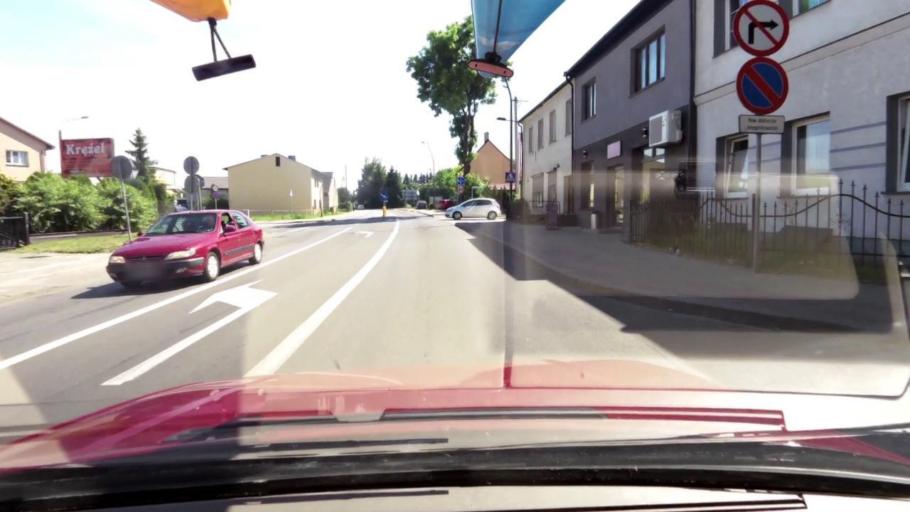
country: PL
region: Pomeranian Voivodeship
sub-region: Powiat slupski
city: Kobylnica
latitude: 54.4388
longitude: 16.9970
